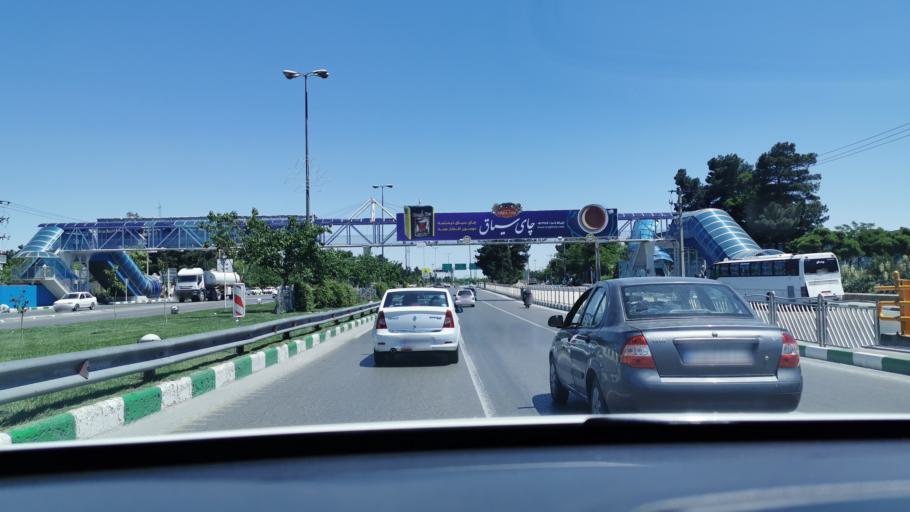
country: IR
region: Razavi Khorasan
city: Mashhad
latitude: 36.2543
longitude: 59.6023
